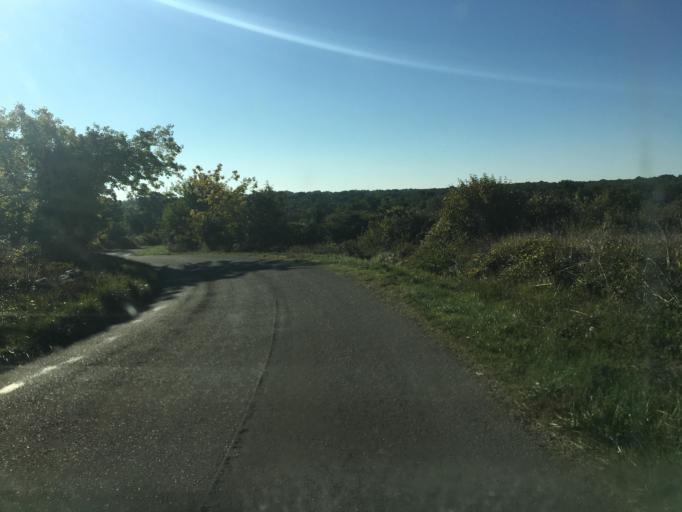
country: FR
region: Languedoc-Roussillon
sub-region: Departement du Gard
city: Barjac
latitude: 44.1829
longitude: 4.3330
